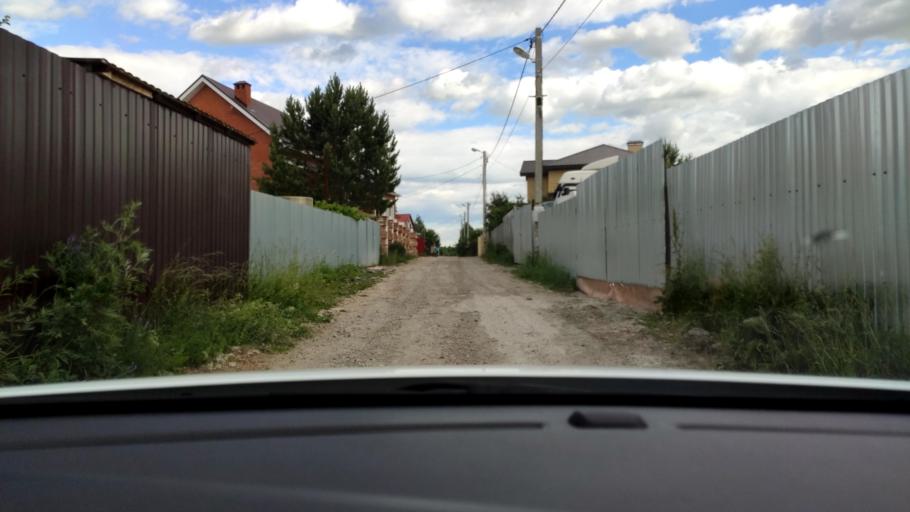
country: RU
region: Tatarstan
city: Stolbishchi
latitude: 55.7611
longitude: 49.3013
